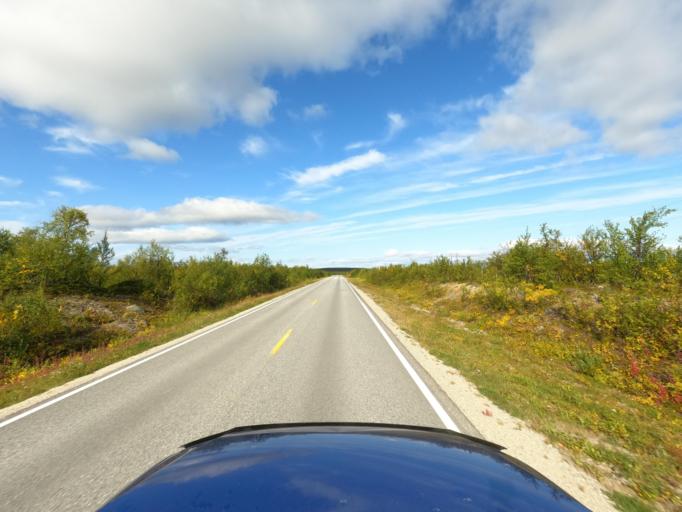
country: NO
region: Finnmark Fylke
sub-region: Karasjok
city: Karasjohka
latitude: 69.6667
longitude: 25.2735
